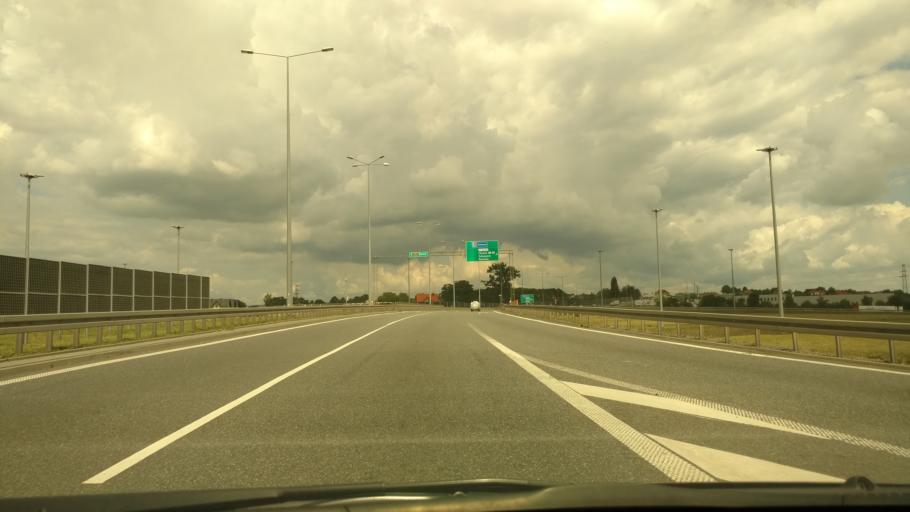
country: PL
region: Lesser Poland Voivodeship
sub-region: Powiat krakowski
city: Modlnica
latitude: 50.1180
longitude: 19.8689
